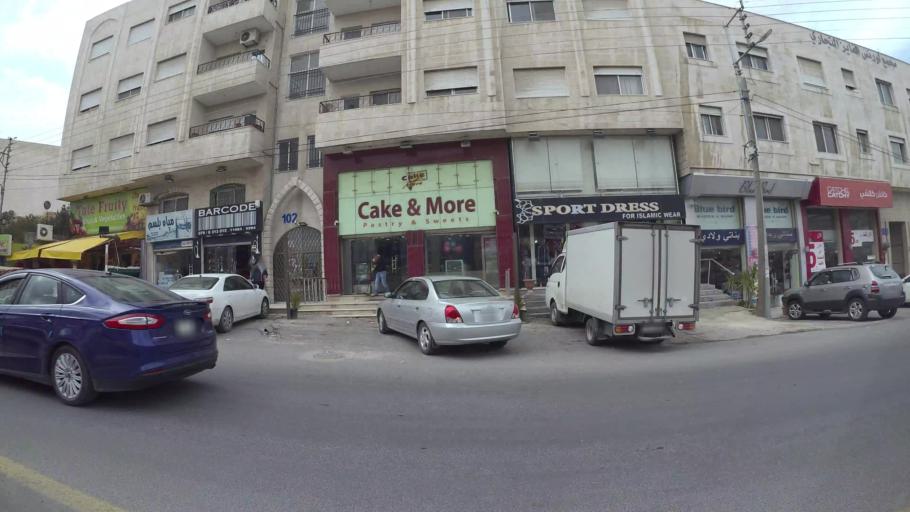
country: JO
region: Amman
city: Umm as Summaq
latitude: 31.8879
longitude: 35.8575
